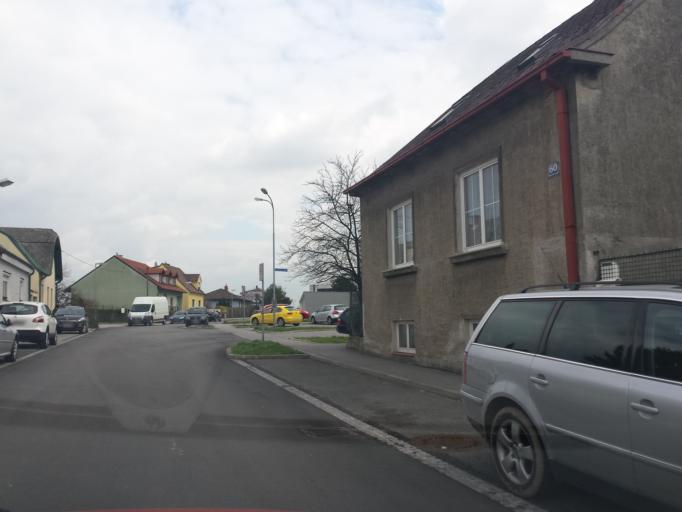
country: AT
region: Lower Austria
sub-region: Politischer Bezirk Bruck an der Leitha
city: Hainburg an der Donau
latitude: 48.1450
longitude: 16.9545
